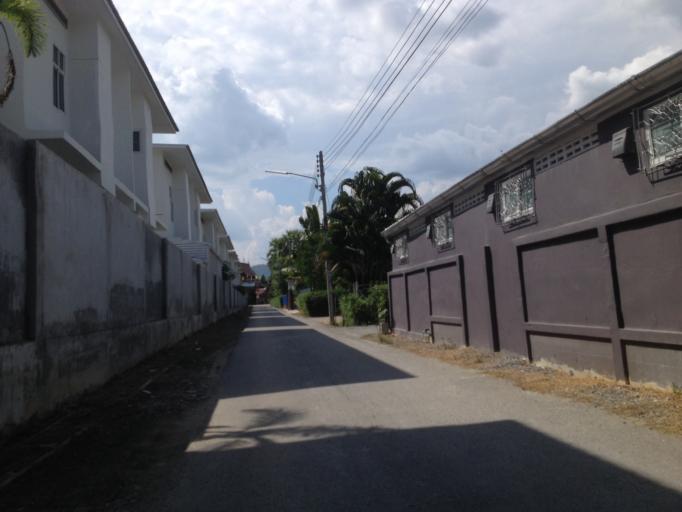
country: TH
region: Chiang Mai
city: Hang Dong
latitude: 18.7263
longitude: 98.9259
